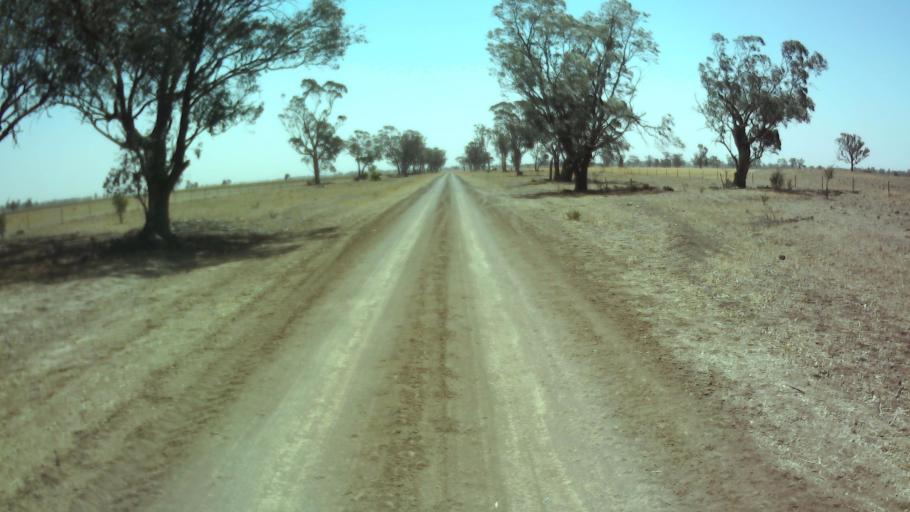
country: AU
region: New South Wales
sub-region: Weddin
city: Grenfell
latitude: -34.0058
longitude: 147.8835
